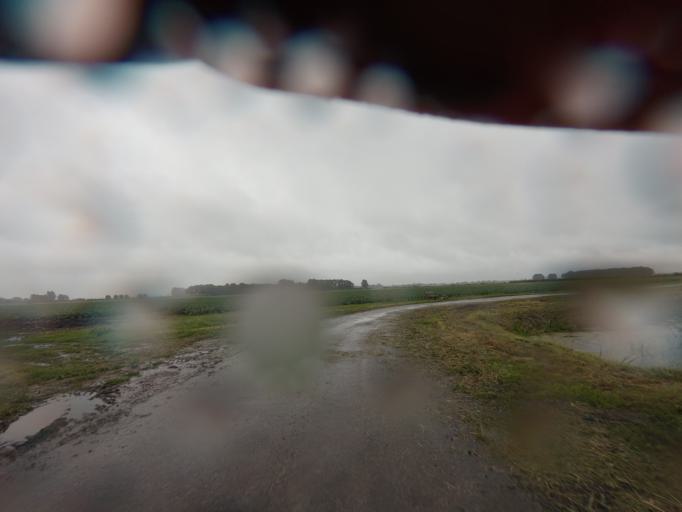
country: NL
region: North Holland
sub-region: Gemeente Medemblik
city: Opperdoes
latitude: 52.7236
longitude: 5.1042
